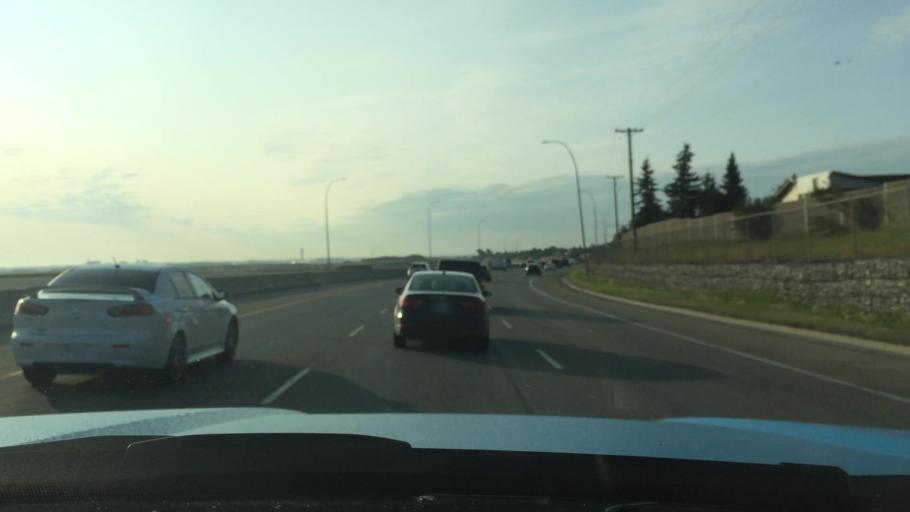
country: CA
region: Alberta
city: Calgary
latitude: 51.1367
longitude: -114.0770
